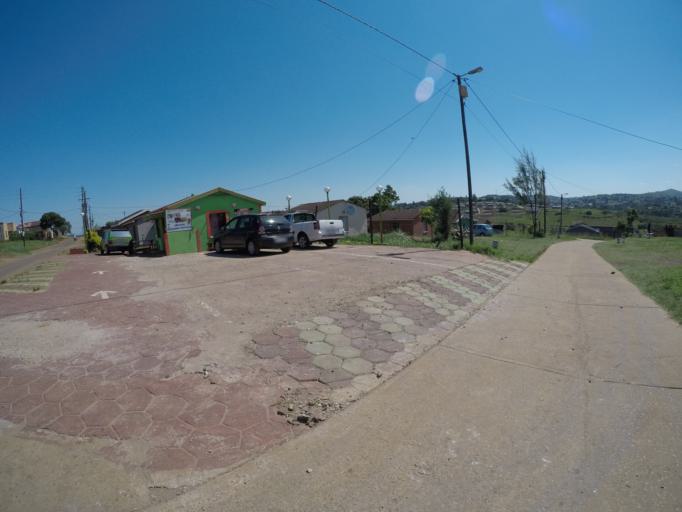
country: ZA
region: KwaZulu-Natal
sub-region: uThungulu District Municipality
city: Empangeni
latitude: -28.7685
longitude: 31.8767
